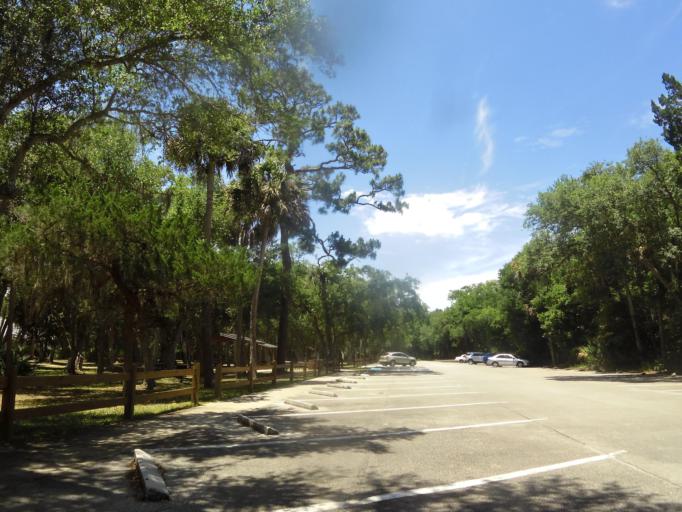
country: US
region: Florida
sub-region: Flagler County
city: Palm Coast
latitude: 29.6259
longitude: -81.2066
